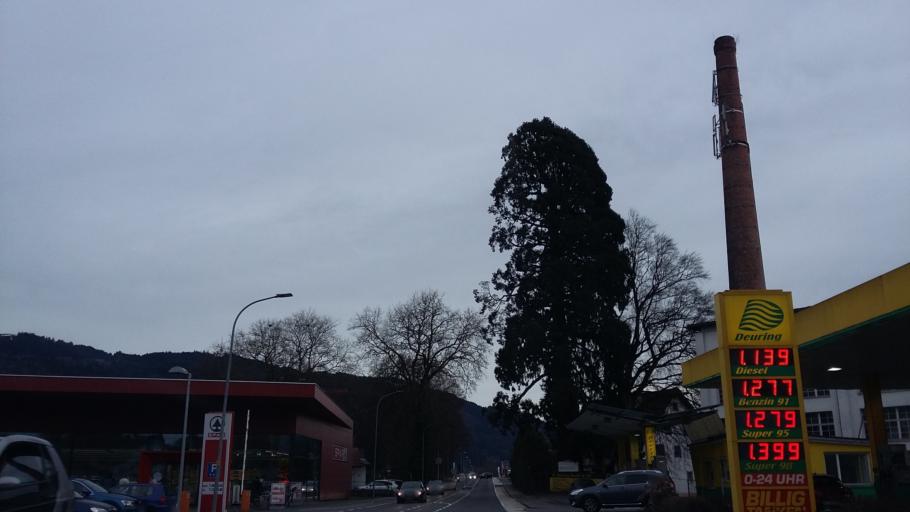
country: AT
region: Vorarlberg
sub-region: Politischer Bezirk Bregenz
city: Lochau
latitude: 47.5356
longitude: 9.7382
